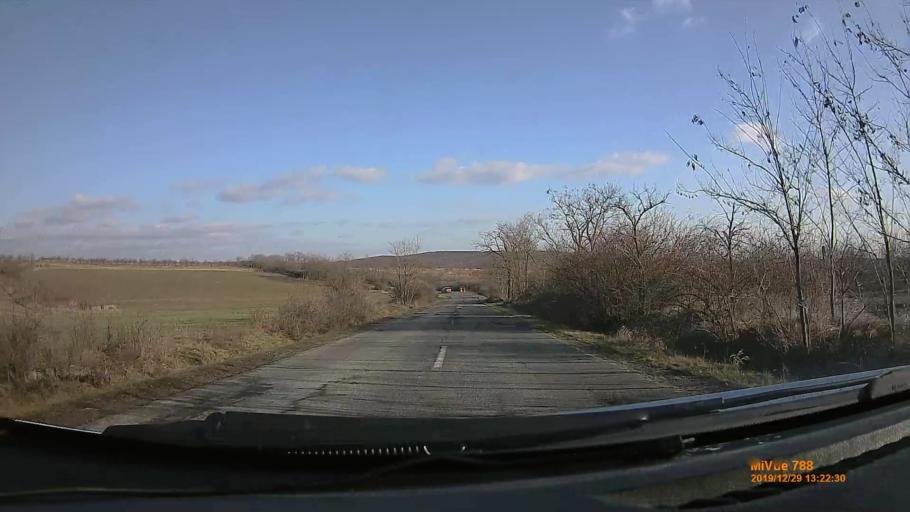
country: HU
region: Heves
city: Domoszlo
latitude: 47.8480
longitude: 20.1576
